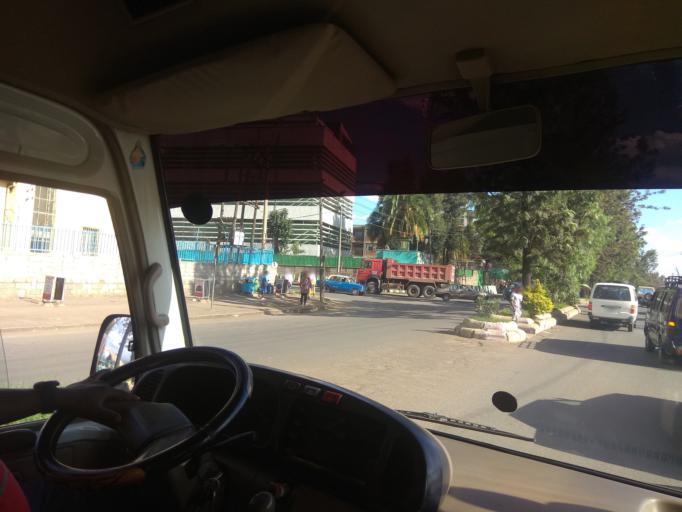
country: ET
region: Adis Abeba
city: Addis Ababa
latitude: 9.0191
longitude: 38.7466
